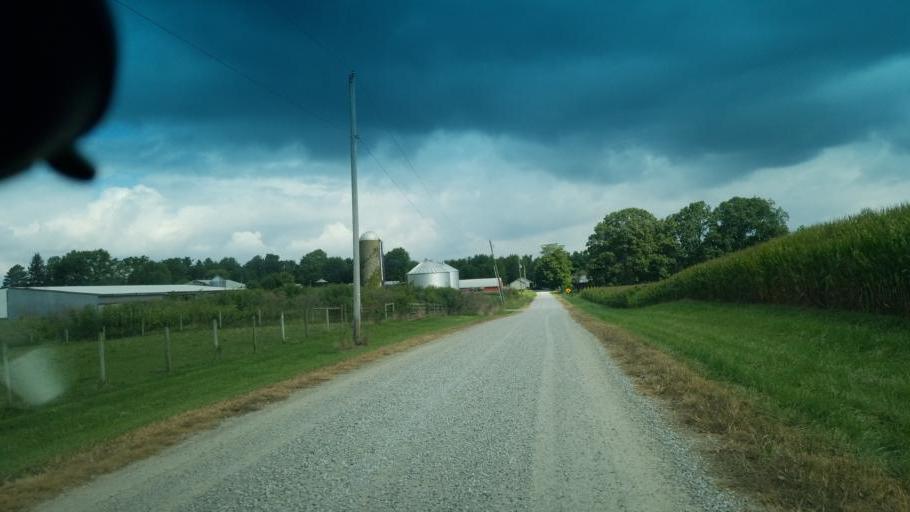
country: US
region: Ohio
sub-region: Knox County
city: Centerburg
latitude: 40.2712
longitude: -82.6719
